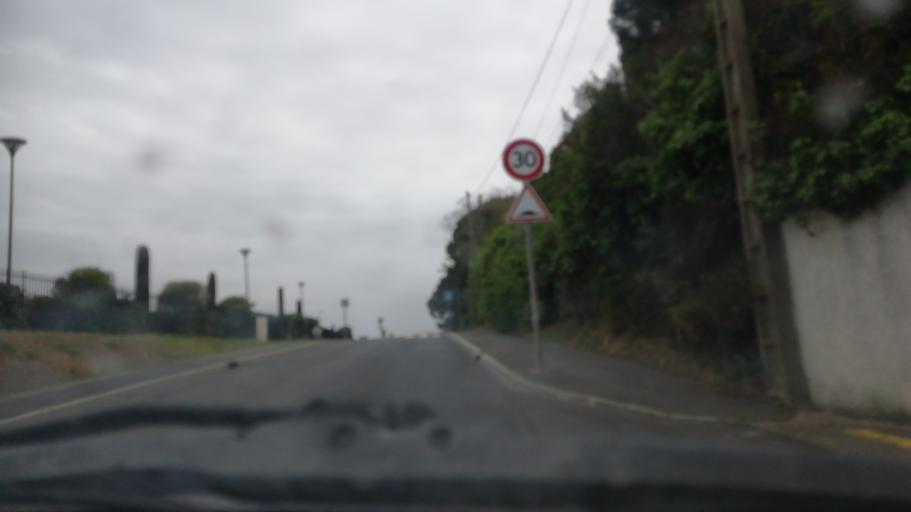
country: FR
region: Languedoc-Roussillon
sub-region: Departement de l'Herault
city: Boujan-sur-Libron
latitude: 43.3672
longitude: 3.2531
